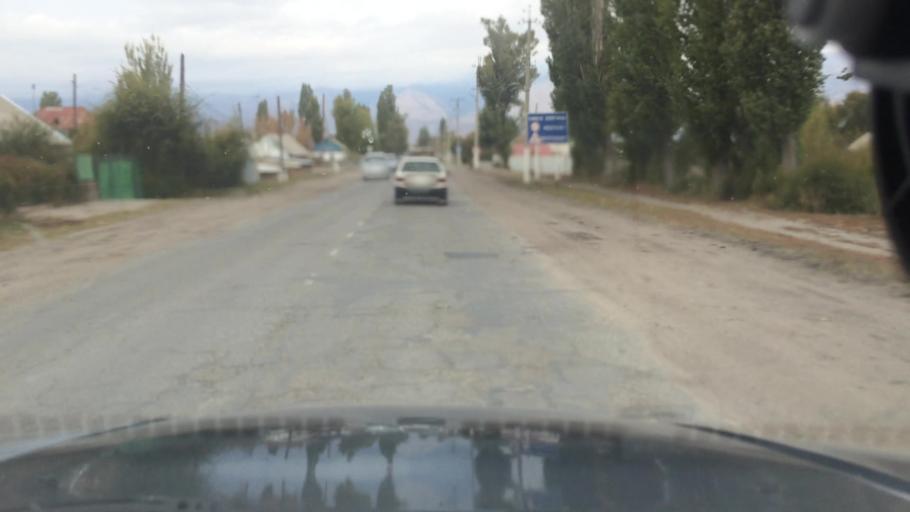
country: KG
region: Ysyk-Koel
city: Tyup
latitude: 42.7231
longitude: 78.3665
